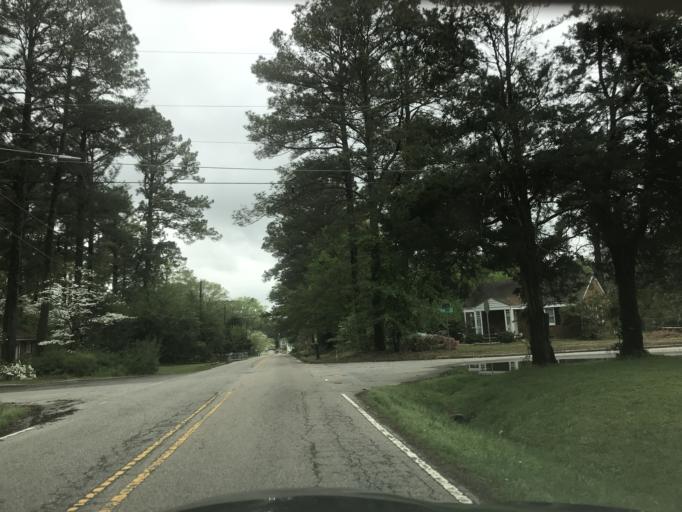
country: US
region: North Carolina
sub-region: Wake County
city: Raleigh
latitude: 35.7480
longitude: -78.6580
